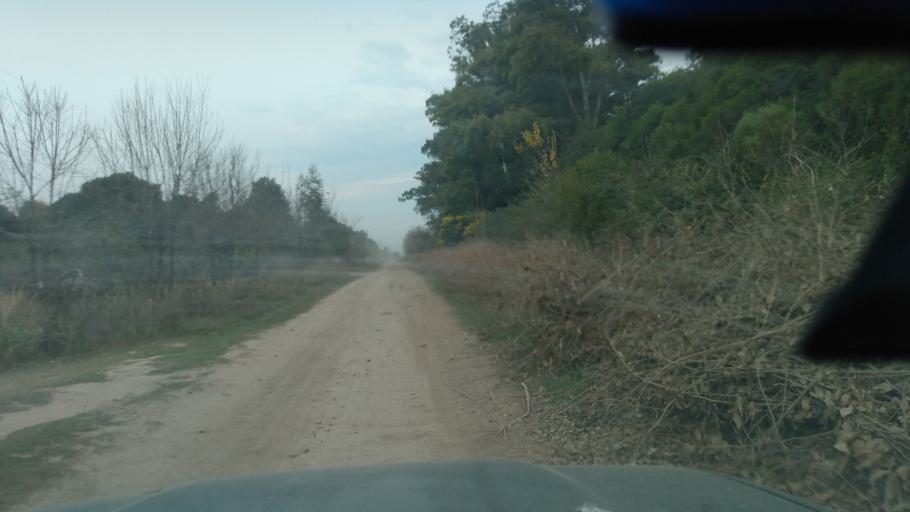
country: AR
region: Buenos Aires
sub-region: Partido de Lujan
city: Lujan
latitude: -34.5516
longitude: -59.1516
